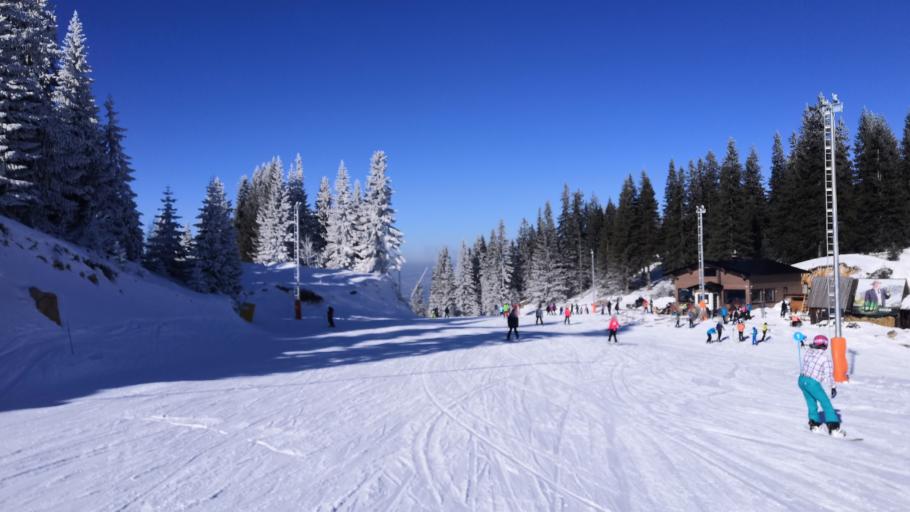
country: BA
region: Republika Srpska
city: Koran
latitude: 43.7289
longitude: 18.5658
